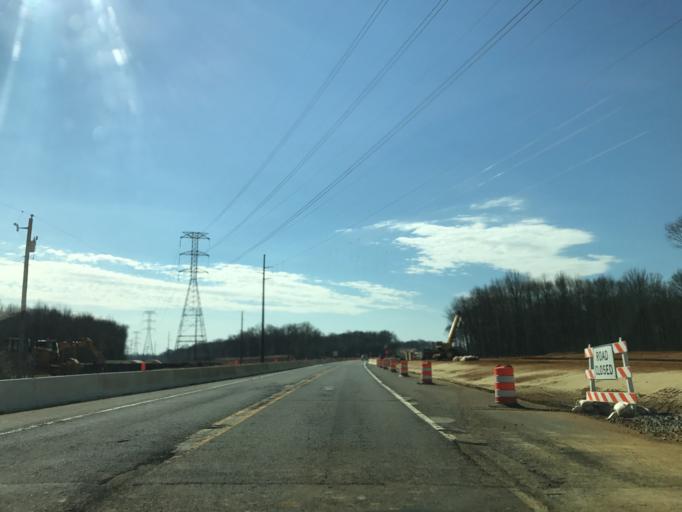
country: US
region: Delaware
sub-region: New Castle County
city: Middletown
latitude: 39.4163
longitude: -75.7658
